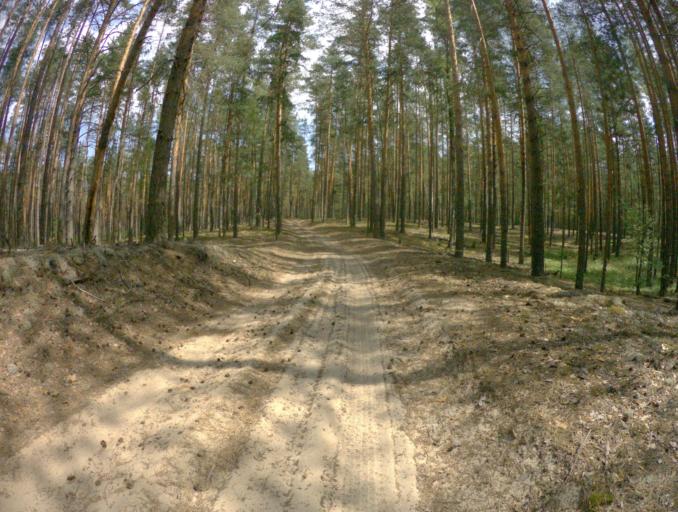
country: RU
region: Ivanovo
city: Talitsy
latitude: 56.3928
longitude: 42.3530
